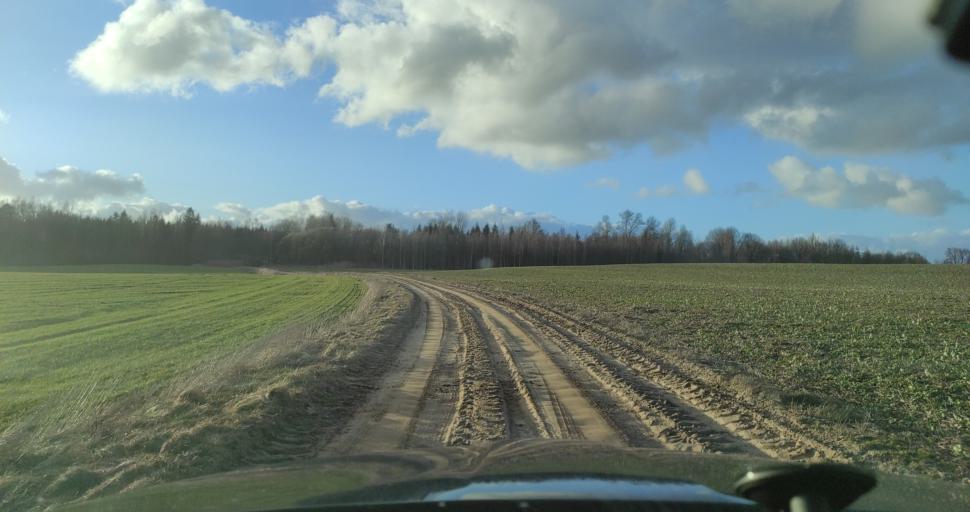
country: LV
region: Aizpute
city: Aizpute
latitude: 56.8689
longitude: 21.7587
